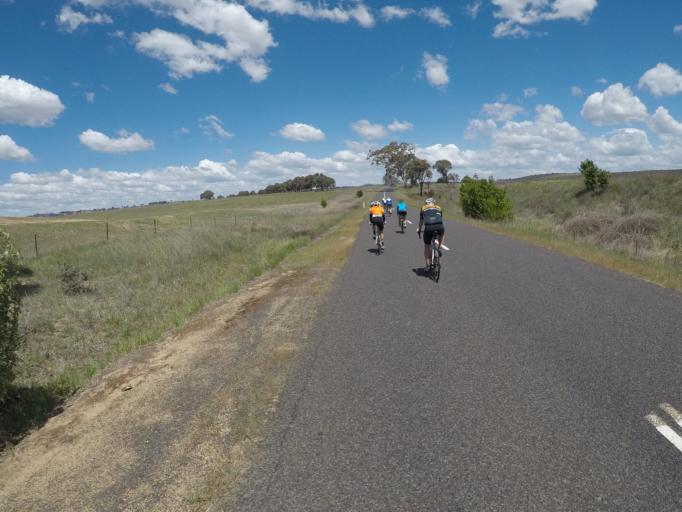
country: AU
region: New South Wales
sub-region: Bathurst Regional
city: Perthville
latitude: -33.5553
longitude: 149.4204
